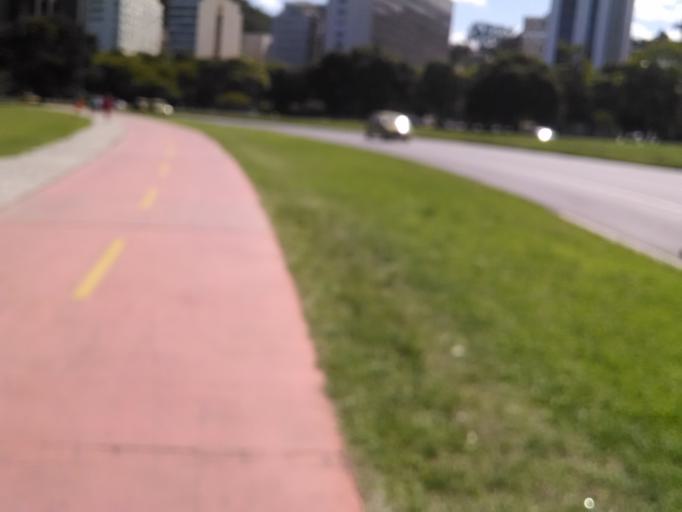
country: BR
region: Rio de Janeiro
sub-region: Rio De Janeiro
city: Rio de Janeiro
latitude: -22.9428
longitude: -43.1780
